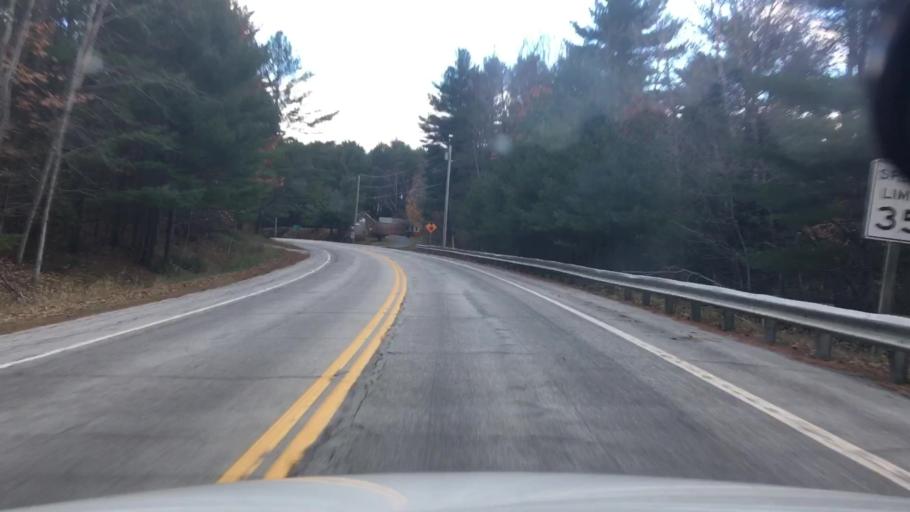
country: US
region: Maine
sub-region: Somerset County
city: Pittsfield
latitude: 44.8273
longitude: -69.4105
